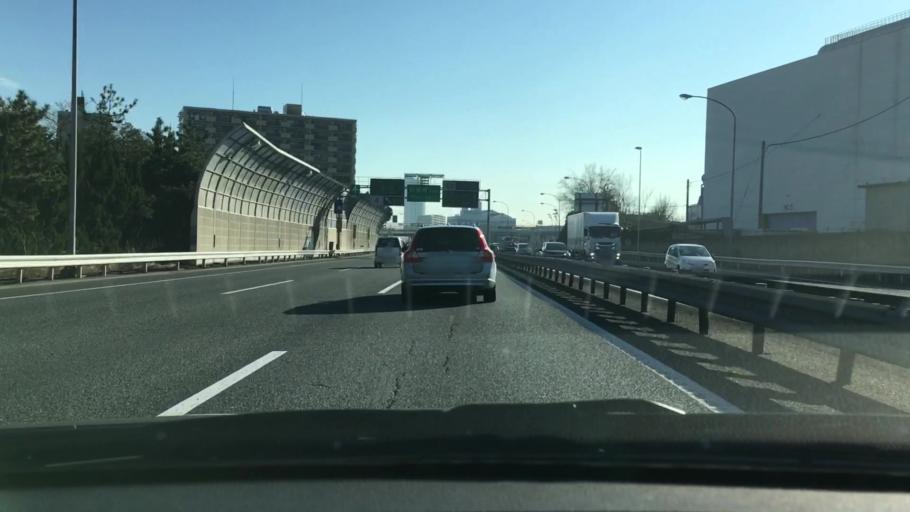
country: JP
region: Chiba
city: Funabashi
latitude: 35.7003
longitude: 139.9630
